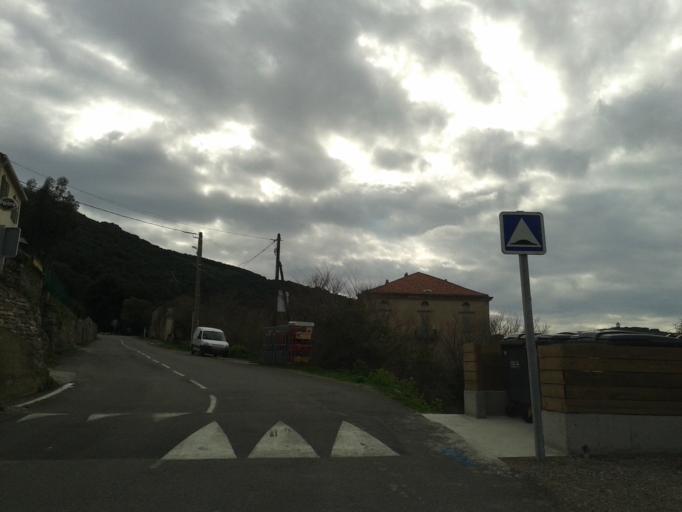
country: FR
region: Corsica
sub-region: Departement de la Haute-Corse
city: Brando
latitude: 42.9751
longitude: 9.3794
